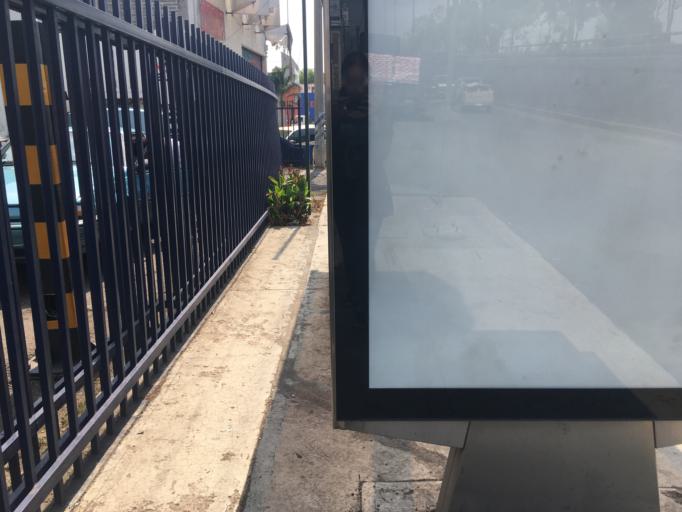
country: MX
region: Michoacan
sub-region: Tarimbaro
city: Real Hacienda (Metropolis)
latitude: 19.7263
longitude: -101.2081
